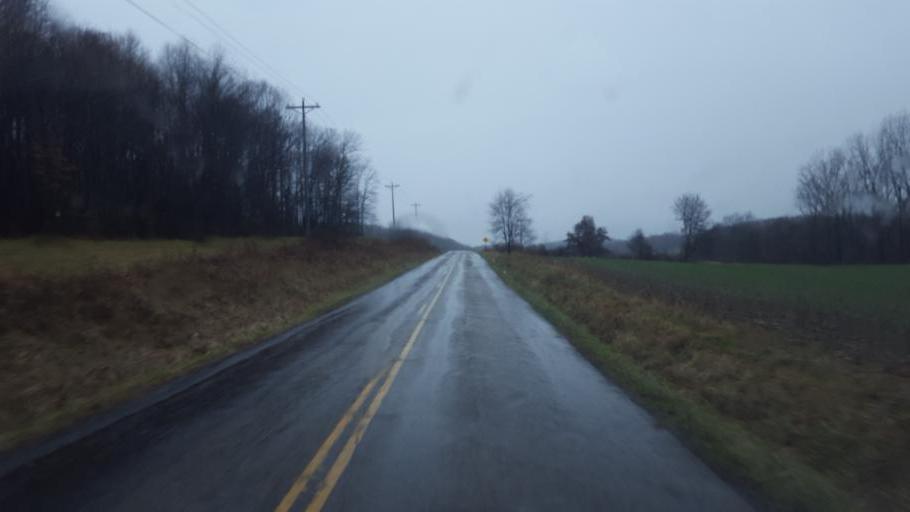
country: US
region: Ohio
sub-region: Knox County
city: Gambier
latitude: 40.4397
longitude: -82.4002
